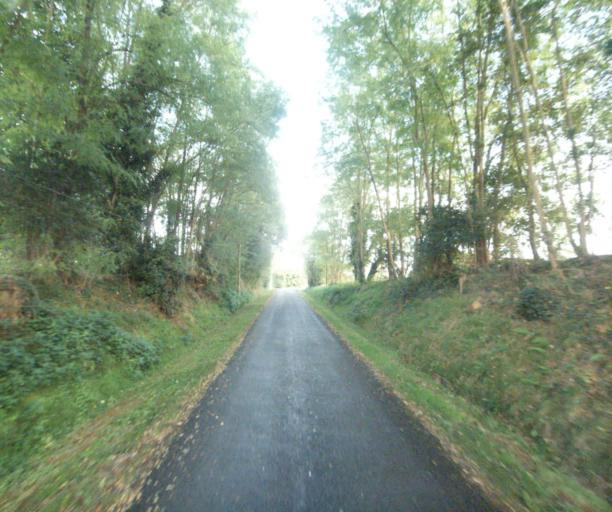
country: FR
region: Midi-Pyrenees
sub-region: Departement du Gers
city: Le Houga
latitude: 43.8425
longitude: -0.1240
